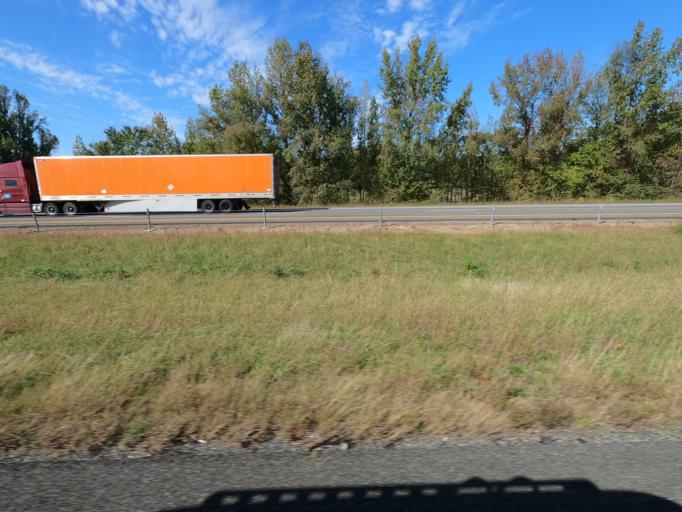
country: US
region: Tennessee
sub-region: Haywood County
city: Brownsville
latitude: 35.4862
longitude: -89.2720
